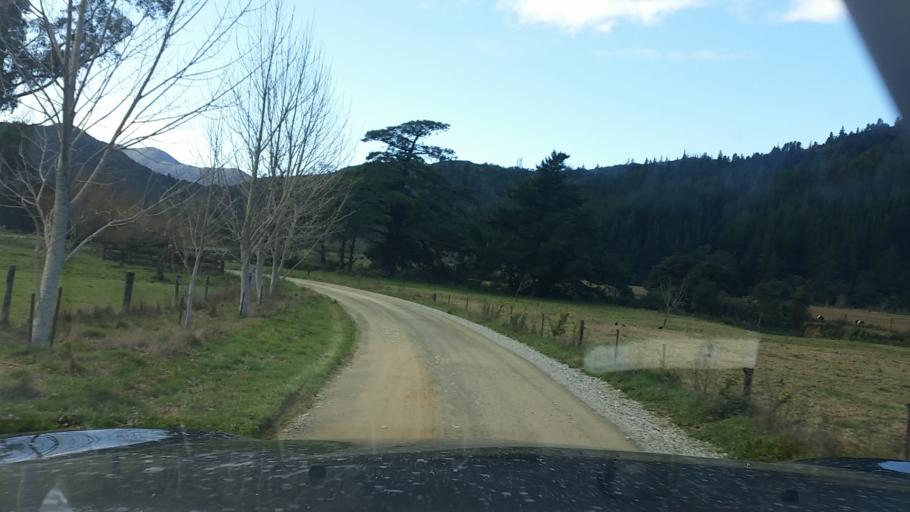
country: NZ
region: Marlborough
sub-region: Marlborough District
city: Picton
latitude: -41.1451
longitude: 174.1350
